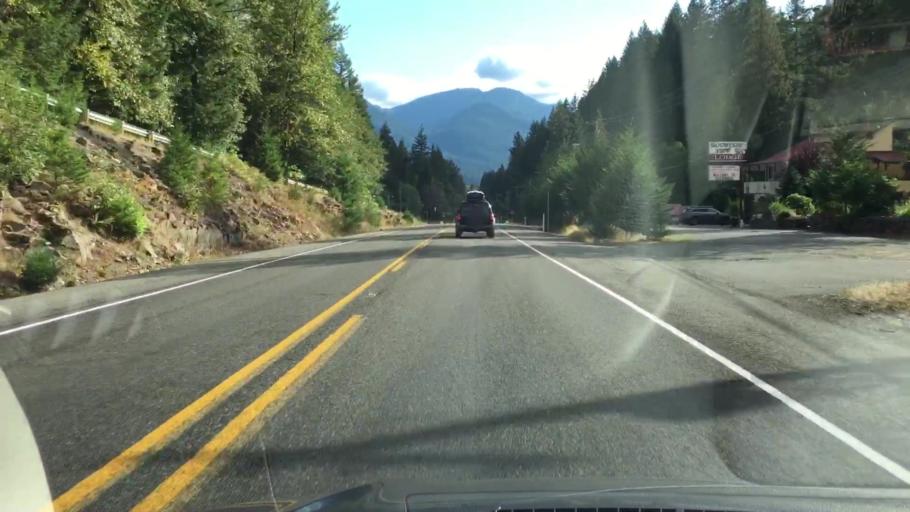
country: US
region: Washington
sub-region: Lewis County
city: Morton
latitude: 46.6173
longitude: -121.6645
